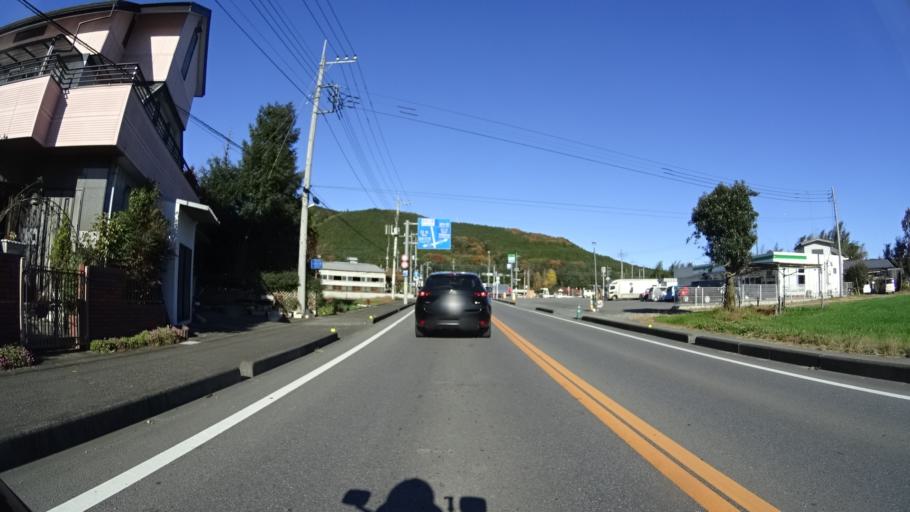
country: JP
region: Tochigi
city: Kanuma
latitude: 36.5949
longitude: 139.7996
